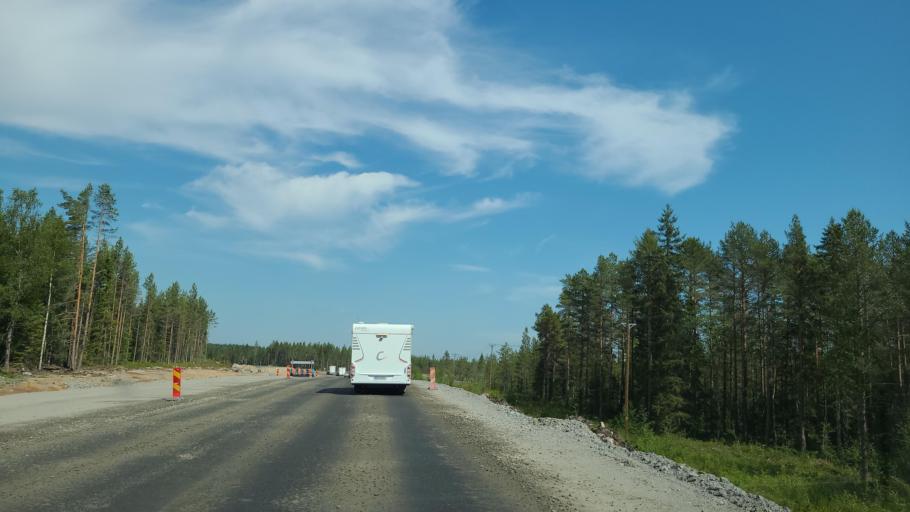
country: SE
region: Vaesterbotten
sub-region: Robertsfors Kommun
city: Robertsfors
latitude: 64.2025
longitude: 21.0147
